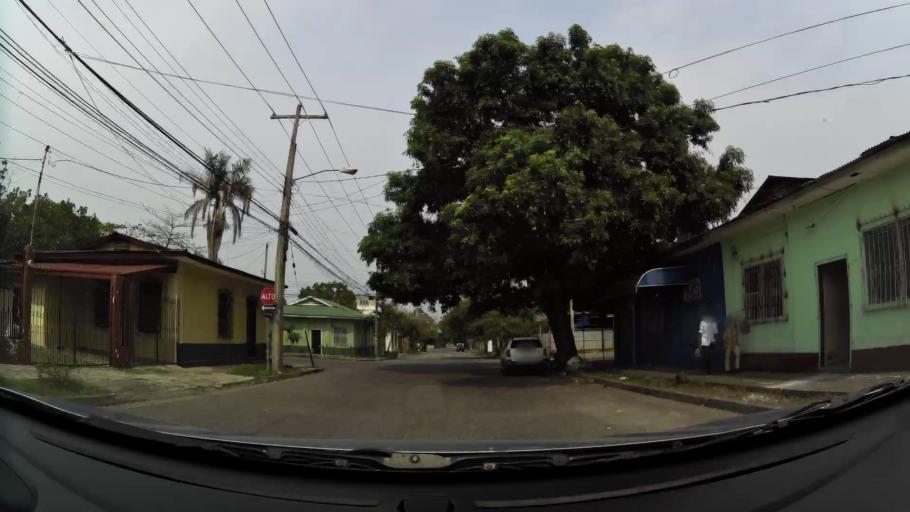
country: HN
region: Cortes
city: San Pedro Sula
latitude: 15.4934
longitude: -88.0304
